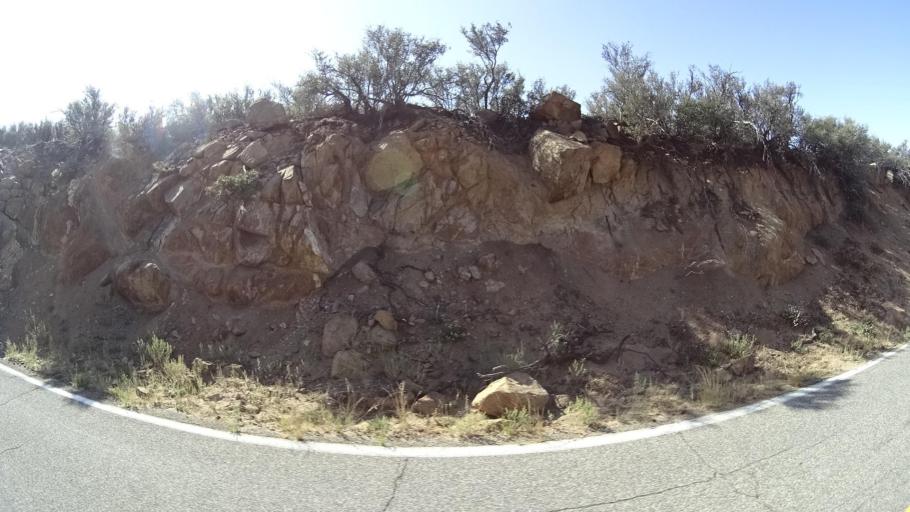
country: US
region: California
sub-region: San Diego County
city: Pine Valley
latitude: 32.9450
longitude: -116.4962
